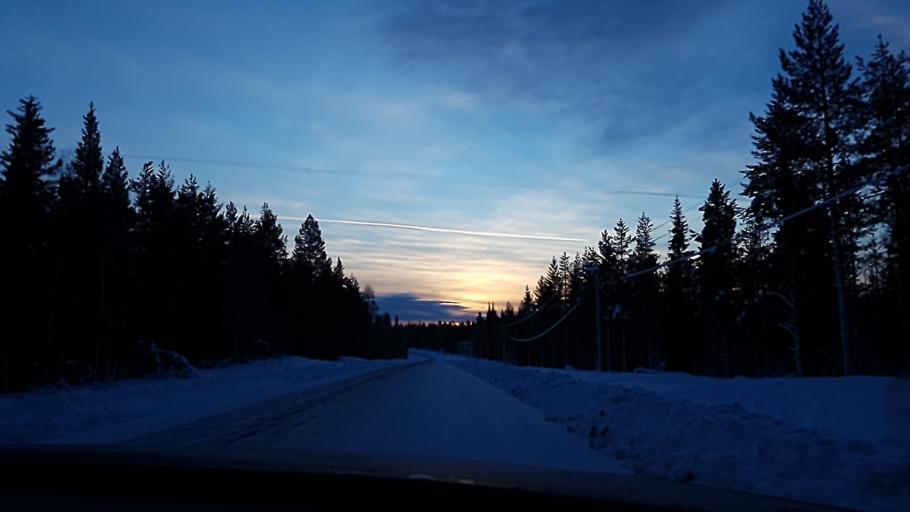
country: SE
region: Norrbotten
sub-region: Jokkmokks Kommun
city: Jokkmokk
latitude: 66.1331
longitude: 20.0009
